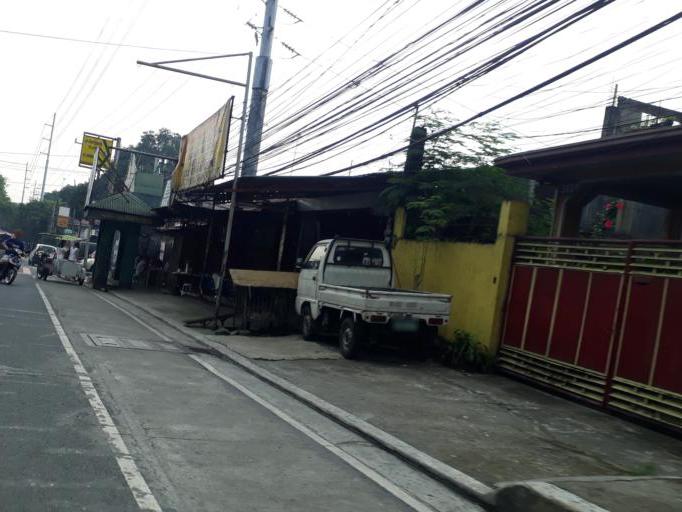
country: PH
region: Calabarzon
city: Bagong Pagasa
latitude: 14.6707
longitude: 121.0522
